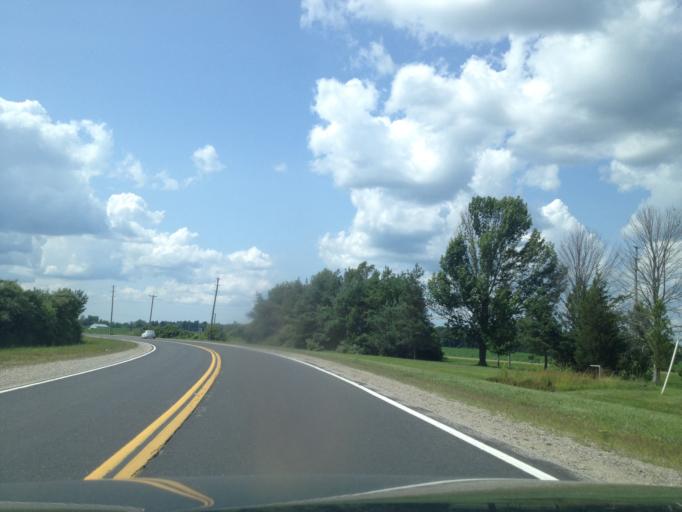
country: CA
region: Ontario
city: Aylmer
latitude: 42.6606
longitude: -80.8107
